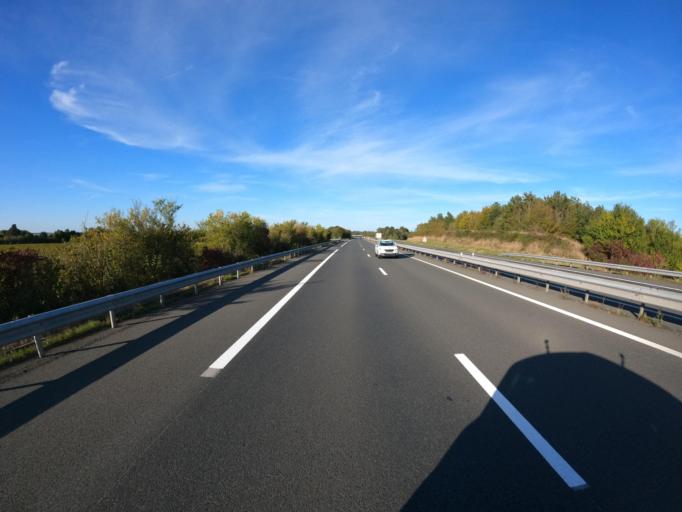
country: FR
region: Pays de la Loire
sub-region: Departement de Maine-et-Loire
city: Saint-Lambert-du-Lattay
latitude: 47.2922
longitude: -0.6134
